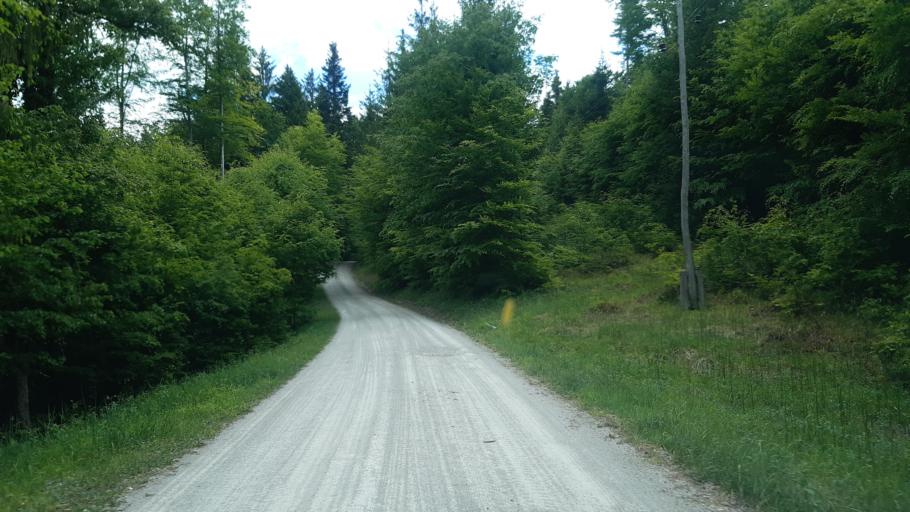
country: SI
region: Dolenjske Toplice
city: Dolenjske Toplice
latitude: 45.6201
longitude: 15.0114
